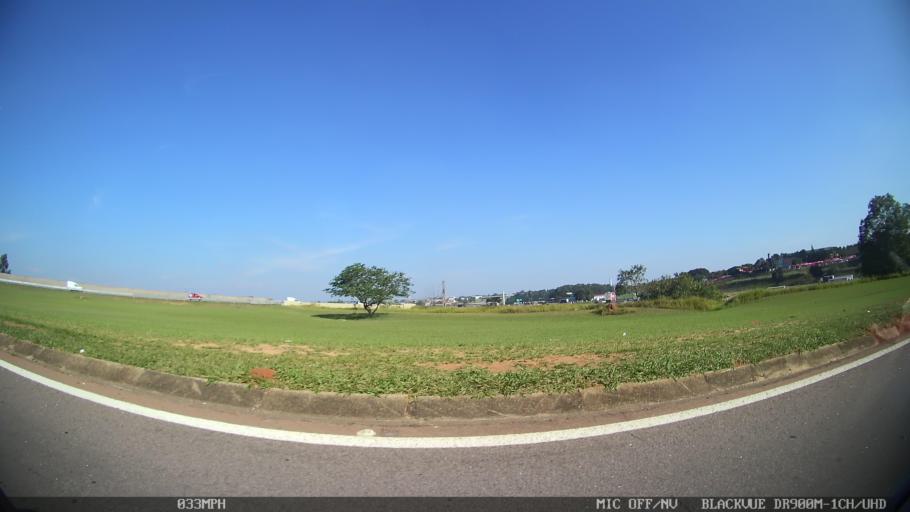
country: BR
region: Sao Paulo
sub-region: Campinas
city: Campinas
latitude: -22.9893
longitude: -47.1087
